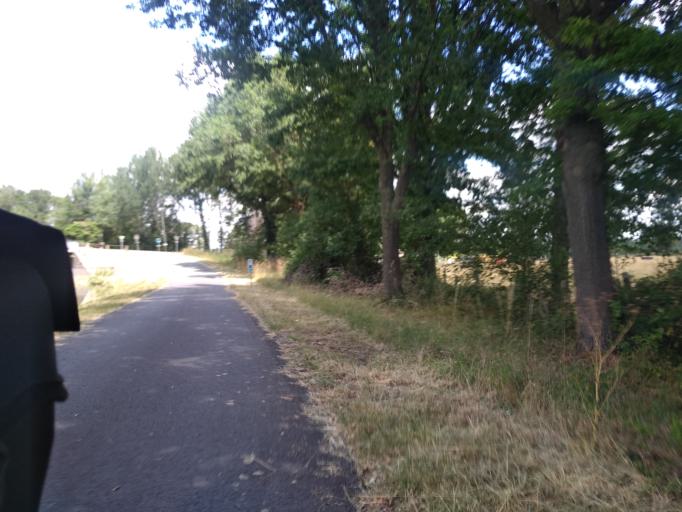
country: FR
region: Rhone-Alpes
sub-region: Departement de la Loire
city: Briennon
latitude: 46.1325
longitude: 4.0825
